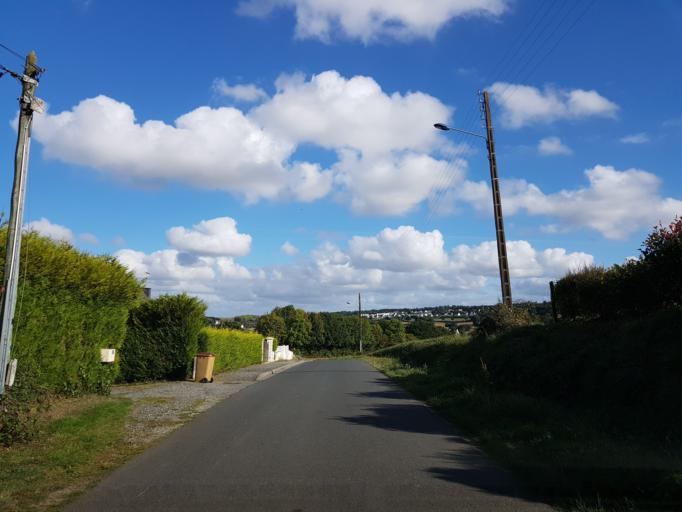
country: FR
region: Brittany
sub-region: Departement des Cotes-d'Armor
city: Pledran
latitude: 48.4677
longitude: -2.7591
